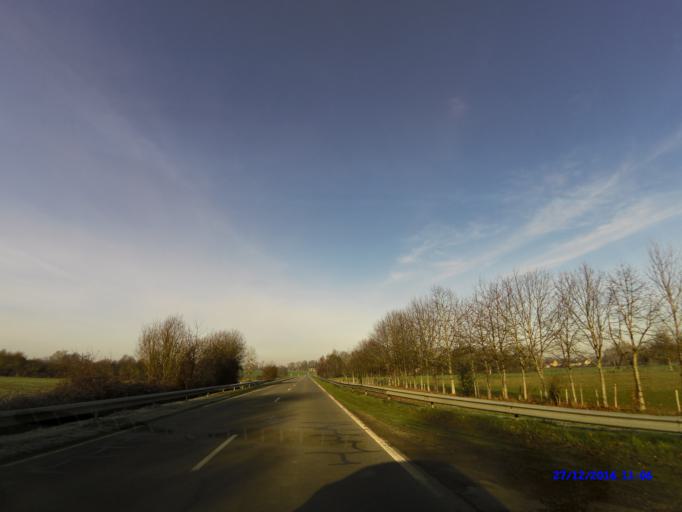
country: FR
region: Brittany
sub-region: Departement d'Ille-et-Vilaine
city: Saint-Erblon
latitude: 48.0079
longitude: -1.6406
